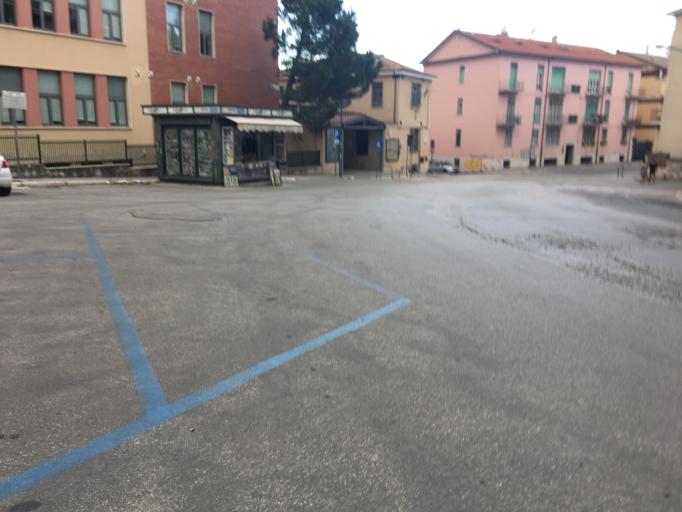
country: IT
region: Molise
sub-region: Provincia di Campobasso
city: Campobasso
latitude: 41.5563
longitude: 14.6569
